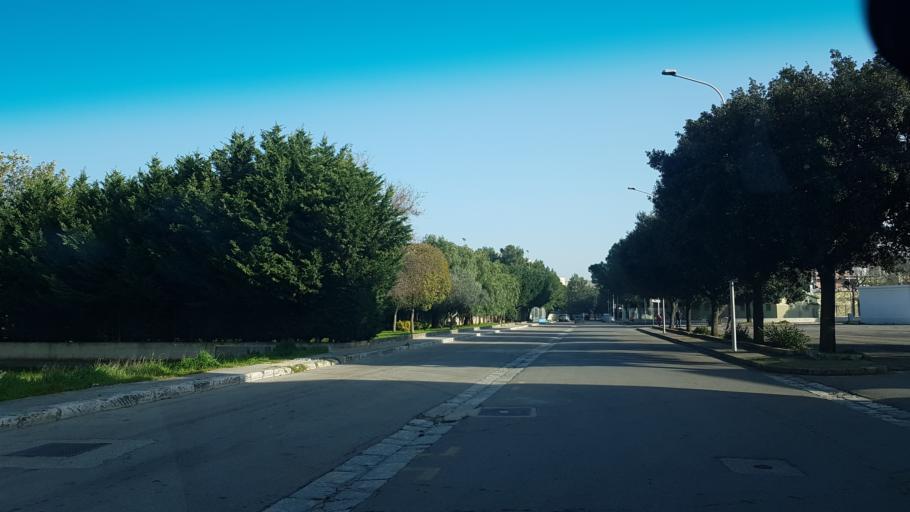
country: IT
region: Apulia
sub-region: Provincia di Brindisi
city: San Vito dei Normanni
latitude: 40.6644
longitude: 17.6979
